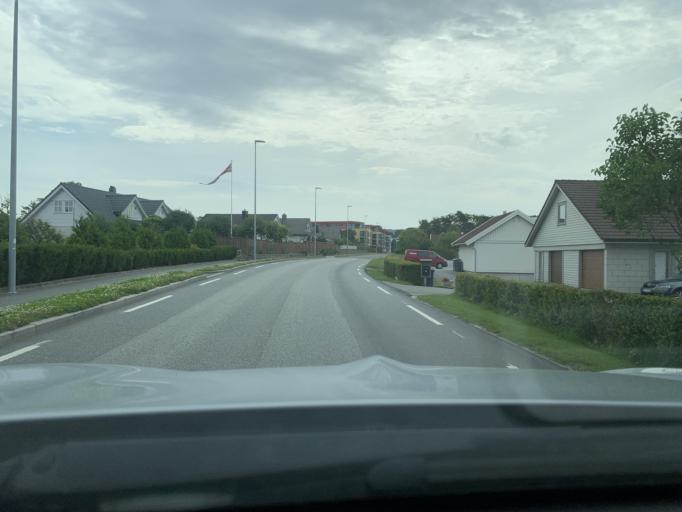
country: NO
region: Rogaland
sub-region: Sandnes
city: Sandnes
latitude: 58.7814
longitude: 5.7180
